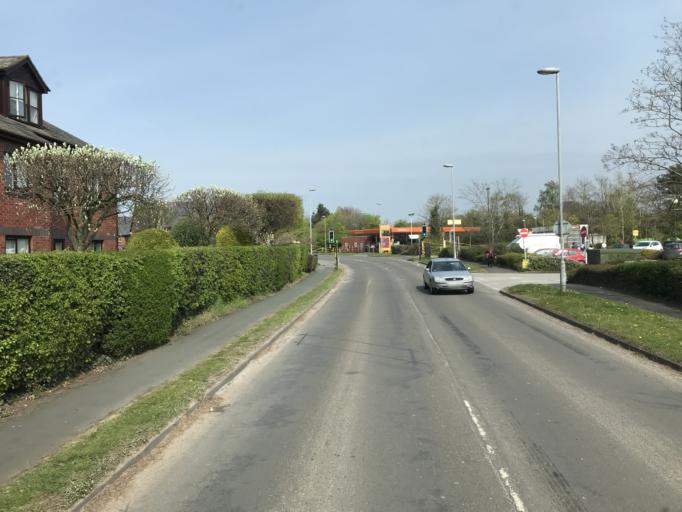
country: GB
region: England
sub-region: Cheshire West and Chester
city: Hoole
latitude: 53.1839
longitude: -2.8565
